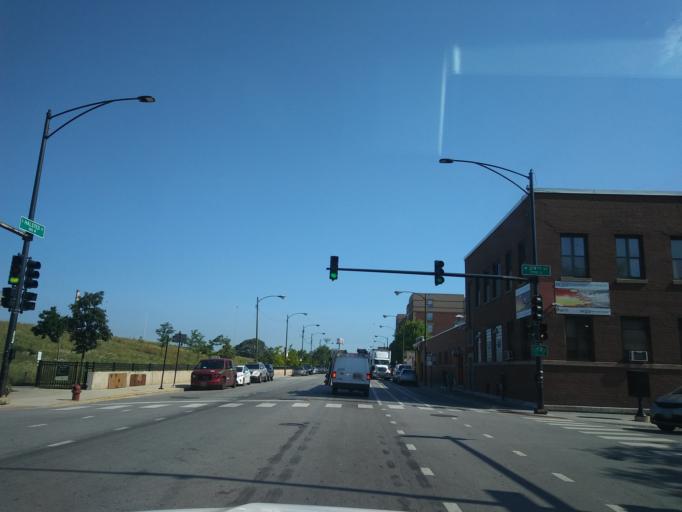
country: US
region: Illinois
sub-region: Cook County
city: Chicago
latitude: 41.8416
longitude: -87.6463
